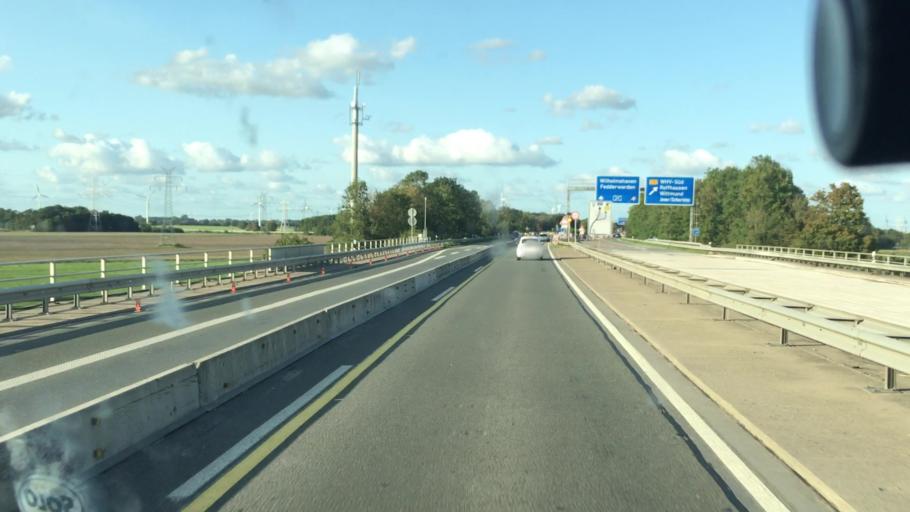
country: DE
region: Lower Saxony
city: Sande
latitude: 53.5193
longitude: 8.0007
